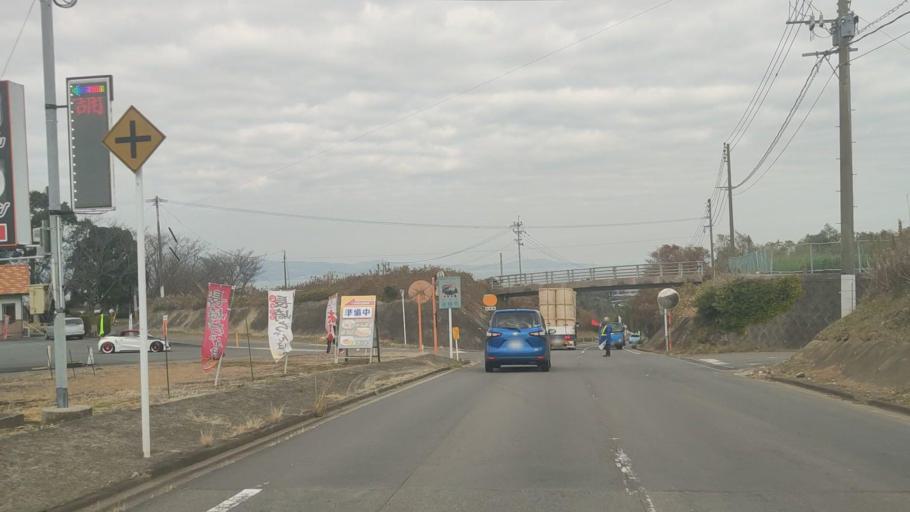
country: JP
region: Nagasaki
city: Shimabara
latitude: 32.8427
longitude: 130.2146
